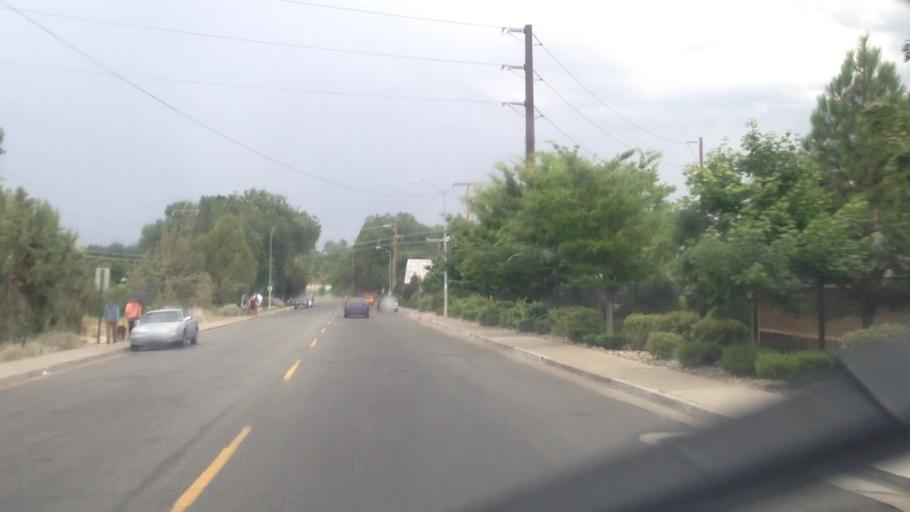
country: US
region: Nevada
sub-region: Washoe County
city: Reno
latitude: 39.5199
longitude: -119.8293
